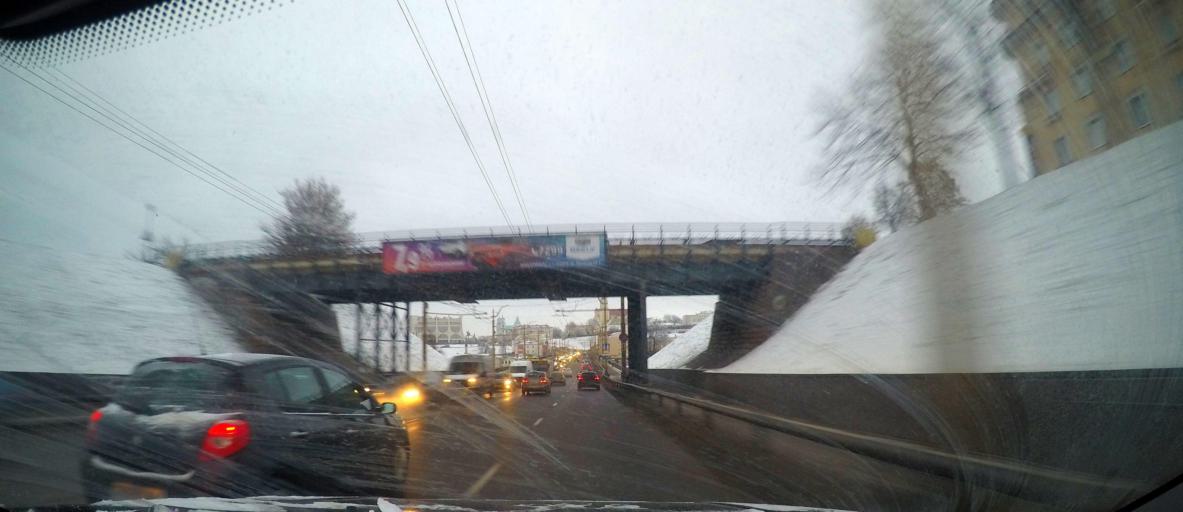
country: BY
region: Grodnenskaya
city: Hrodna
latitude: 53.6708
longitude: 23.8247
